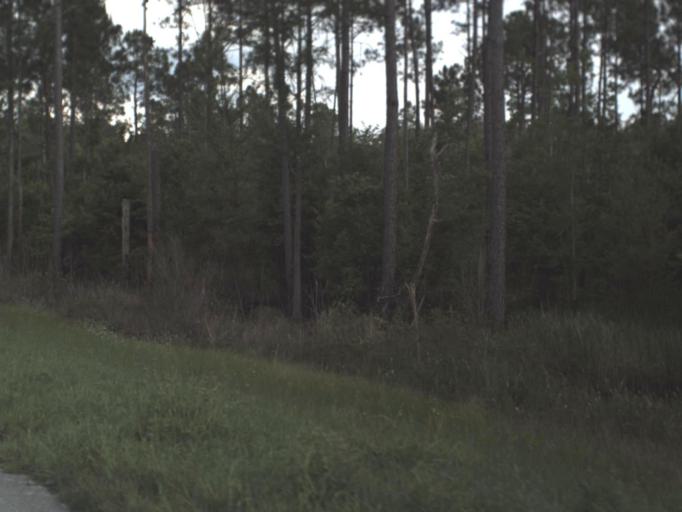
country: US
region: Florida
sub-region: Baker County
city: Macclenny
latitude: 30.5296
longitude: -82.3090
